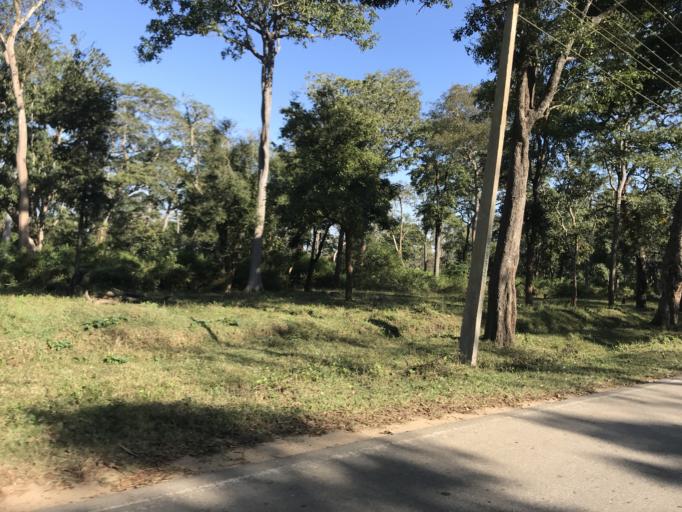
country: IN
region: Karnataka
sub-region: Mysore
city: Heggadadevankote
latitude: 11.9527
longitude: 76.2285
